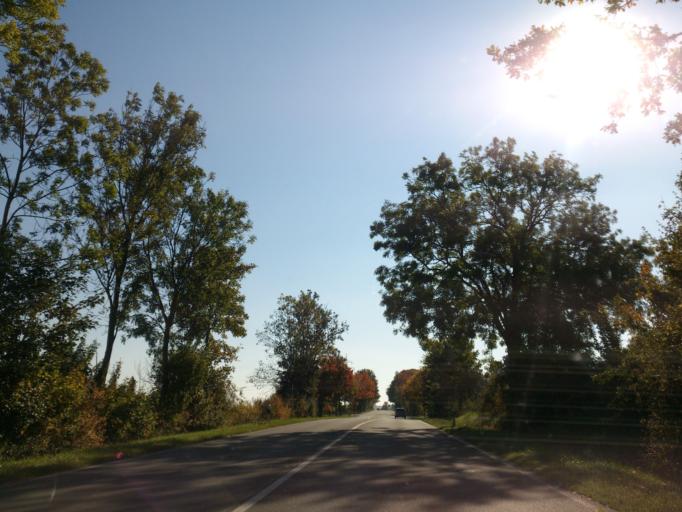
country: DE
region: North Rhine-Westphalia
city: Warburg
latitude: 51.4831
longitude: 9.1763
